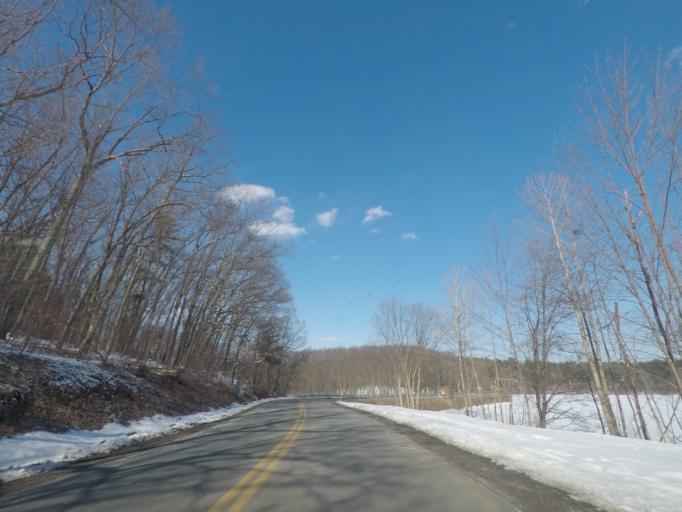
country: US
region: New York
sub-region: Saratoga County
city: Stillwater
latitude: 42.8694
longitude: -73.5838
